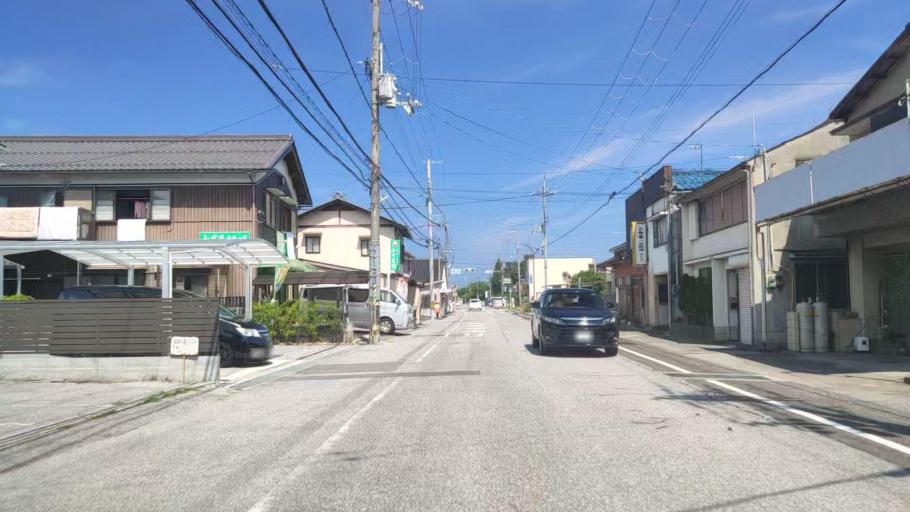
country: JP
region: Shiga Prefecture
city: Hikone
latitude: 35.2734
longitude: 136.2460
